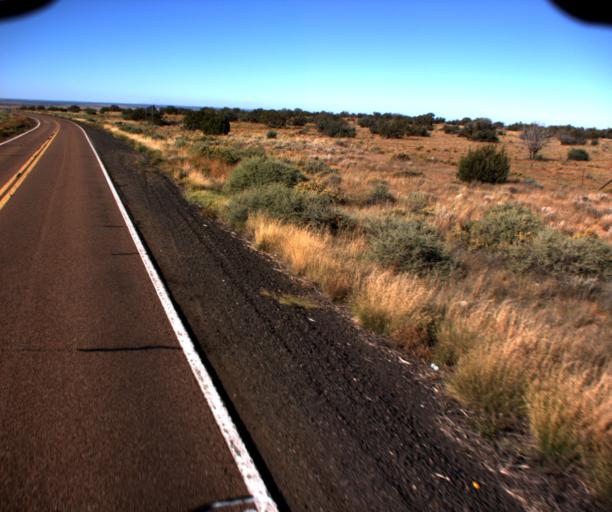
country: US
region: Arizona
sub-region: Navajo County
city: Snowflake
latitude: 34.6439
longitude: -110.3535
